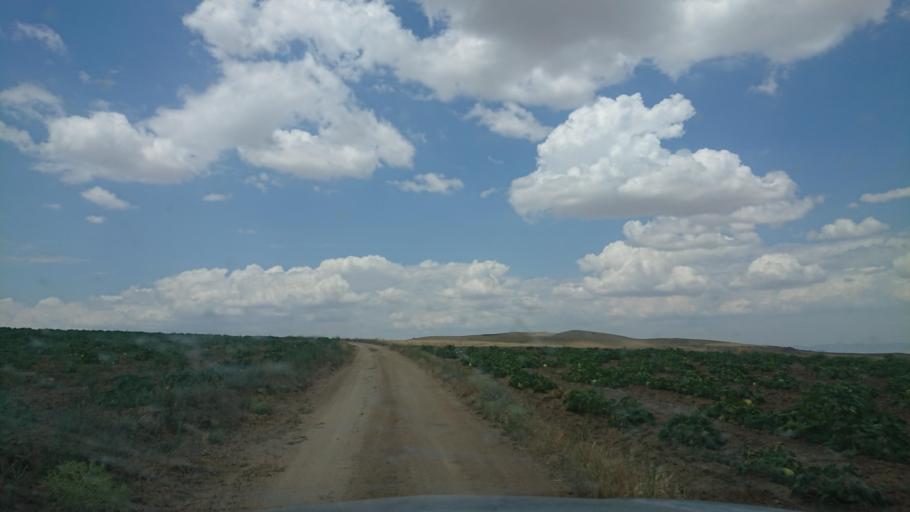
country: TR
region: Aksaray
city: Agacoren
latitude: 38.8965
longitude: 33.8832
